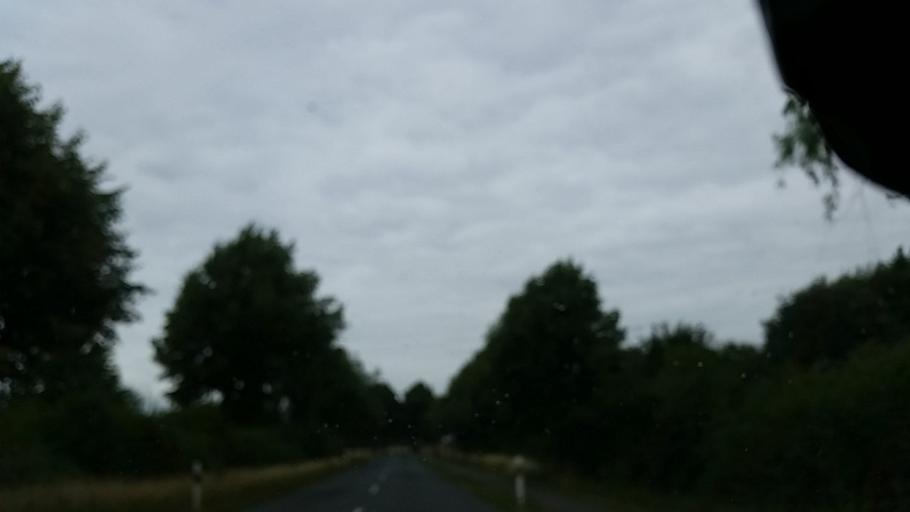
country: DE
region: Lower Saxony
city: Grafhorst
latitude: 52.4350
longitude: 10.9313
